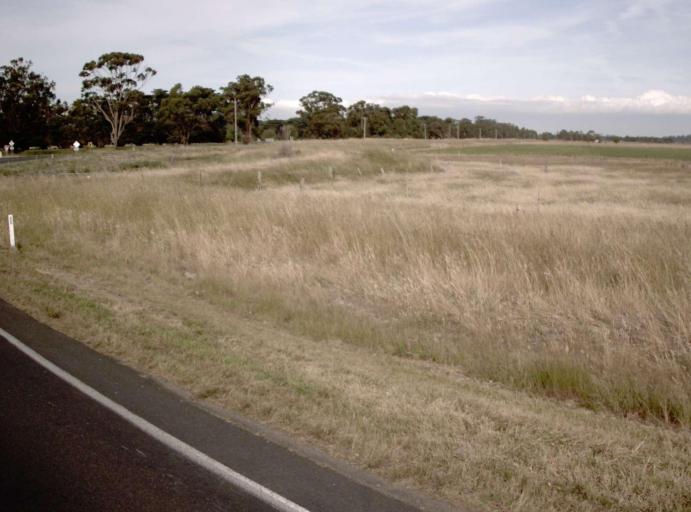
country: AU
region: Victoria
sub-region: Wellington
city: Heyfield
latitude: -38.0126
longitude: 146.6720
